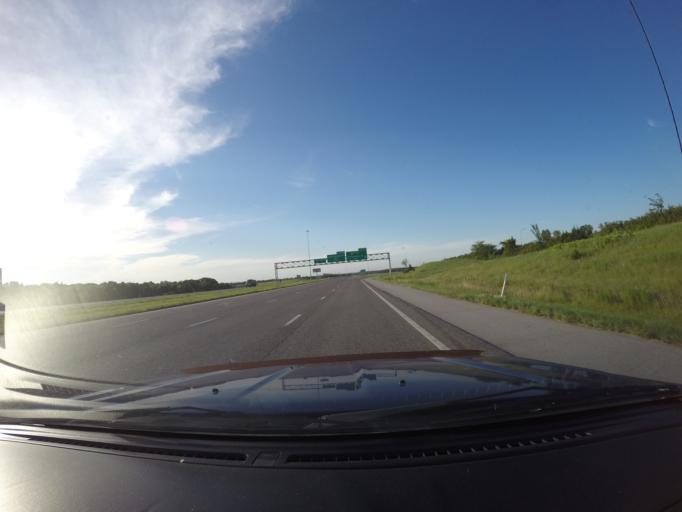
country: US
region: Kansas
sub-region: Wyandotte County
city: Edwardsville
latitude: 39.1375
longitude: -94.8188
